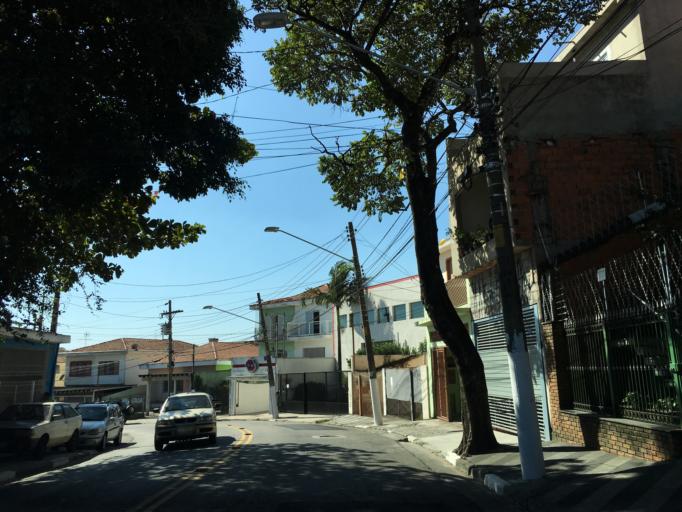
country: BR
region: Sao Paulo
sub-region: Osasco
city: Osasco
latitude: -23.5769
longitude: -46.7612
